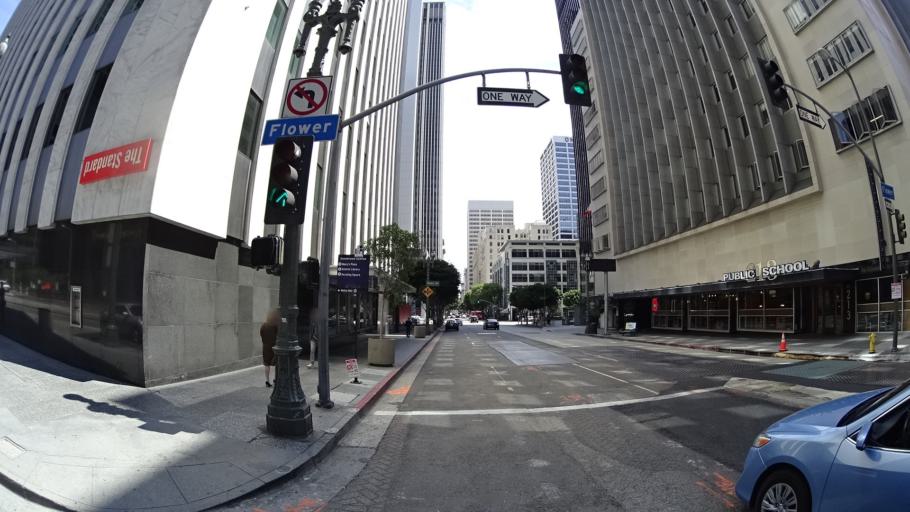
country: US
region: California
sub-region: Los Angeles County
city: Los Angeles
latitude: 34.0501
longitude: -118.2575
